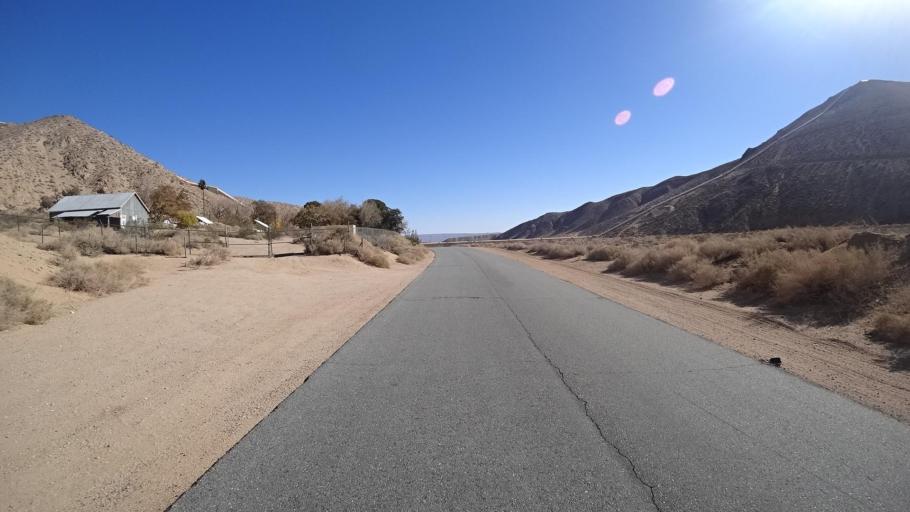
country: US
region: California
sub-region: Kern County
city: California City
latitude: 35.3157
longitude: -118.0475
